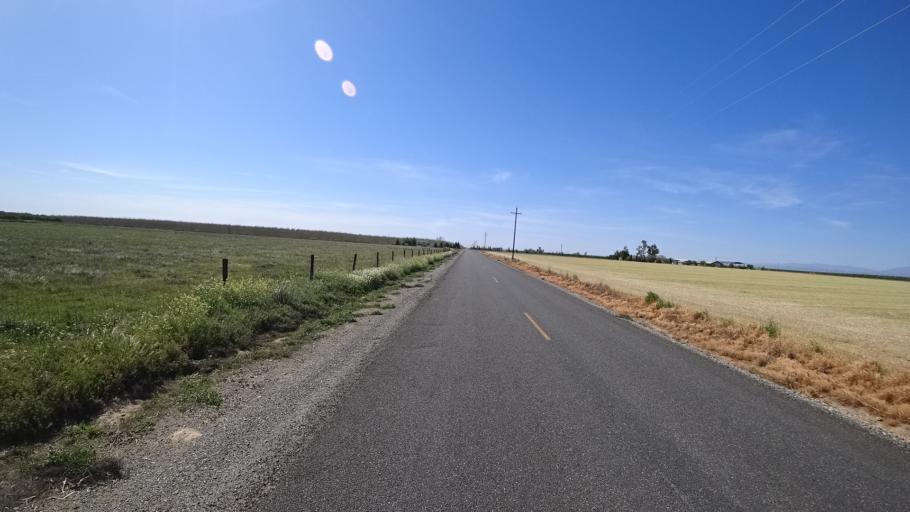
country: US
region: California
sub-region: Glenn County
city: Hamilton City
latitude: 39.6555
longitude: -122.1036
